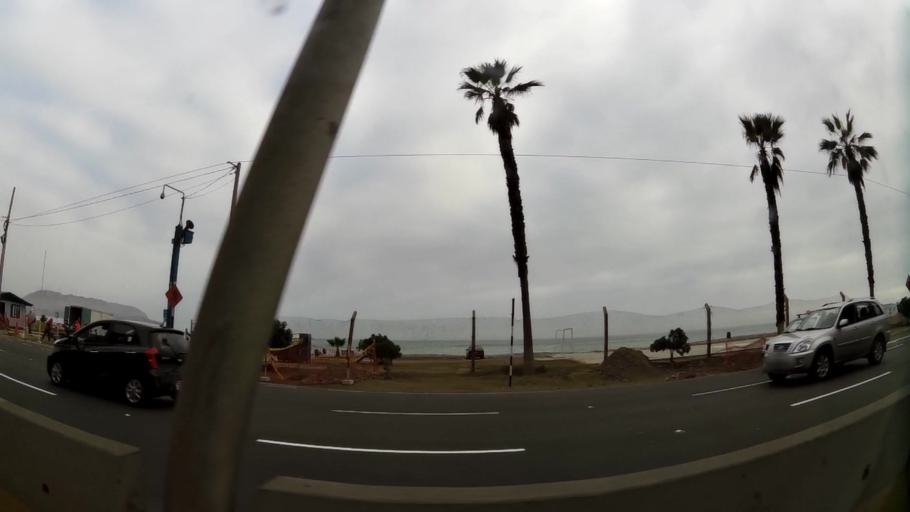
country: PE
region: Lima
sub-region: Lima
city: San Isidro
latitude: -12.1329
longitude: -77.0307
